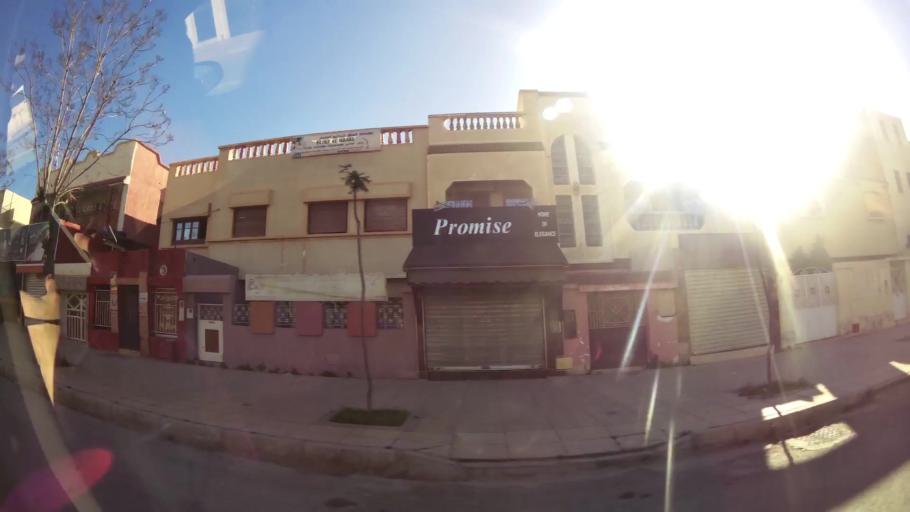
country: MA
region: Oriental
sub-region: Oujda-Angad
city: Oujda
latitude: 34.6589
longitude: -1.9026
